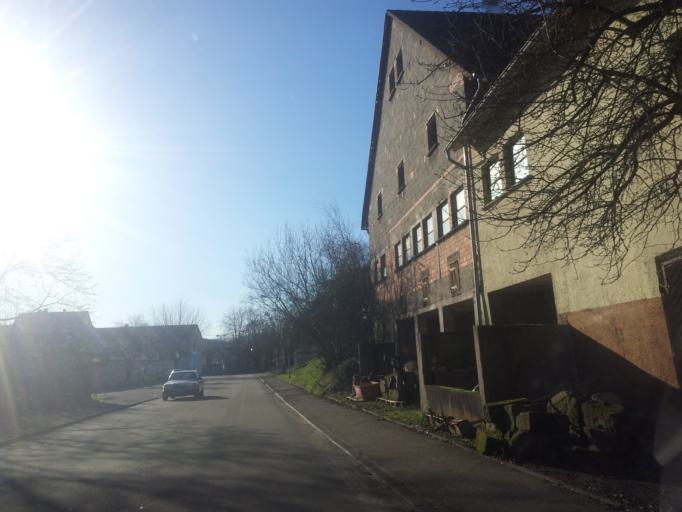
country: DE
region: Baden-Wuerttemberg
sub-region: Regierungsbezirk Stuttgart
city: Lowenstein
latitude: 49.1377
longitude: 9.3836
